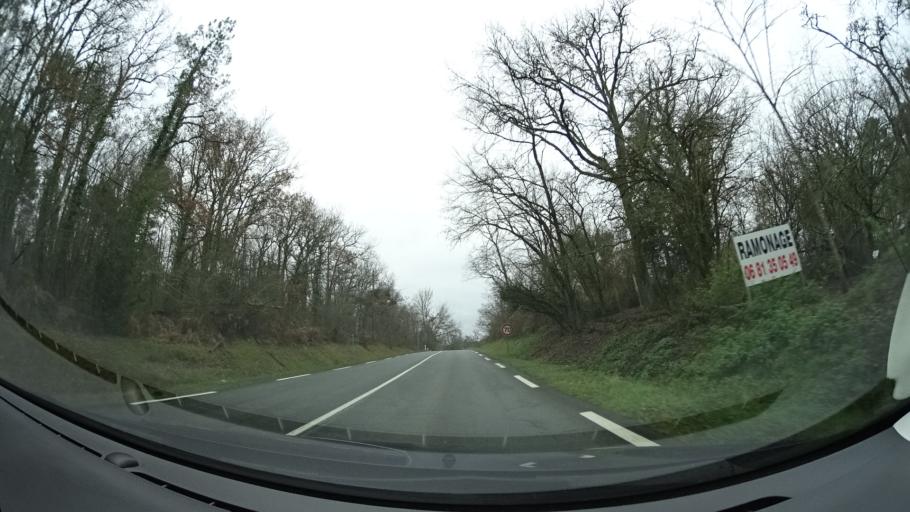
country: FR
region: Aquitaine
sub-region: Departement du Lot-et-Garonne
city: Buzet-sur-Baise
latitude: 44.2356
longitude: 0.2332
